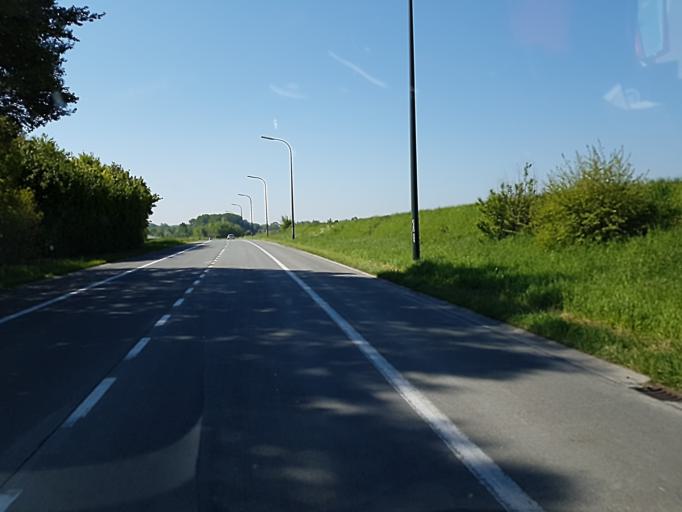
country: BE
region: Wallonia
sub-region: Province du Hainaut
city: Ath
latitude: 50.6747
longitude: 3.7988
